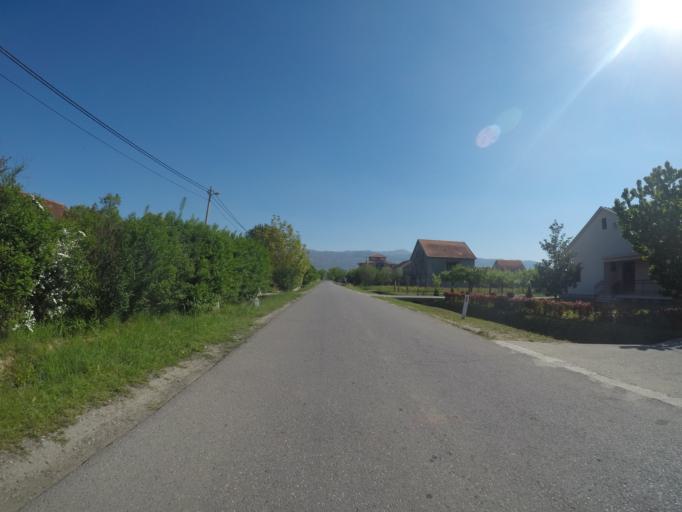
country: ME
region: Danilovgrad
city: Danilovgrad
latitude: 42.5404
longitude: 19.0936
